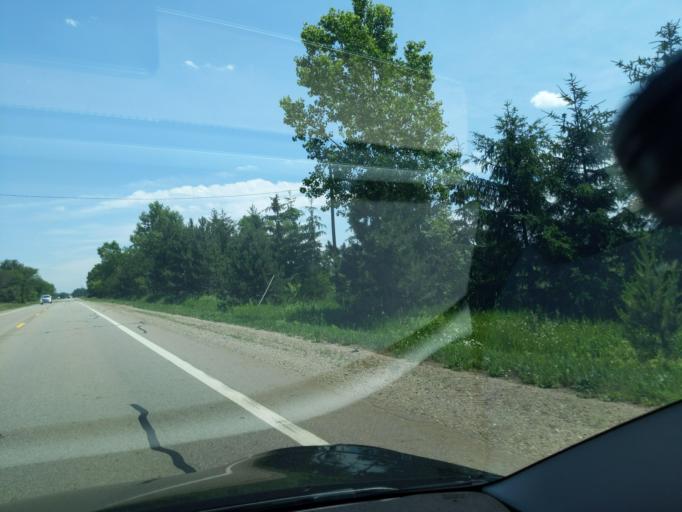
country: US
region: Michigan
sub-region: Clinton County
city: Saint Johns
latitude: 43.0016
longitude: -84.6377
